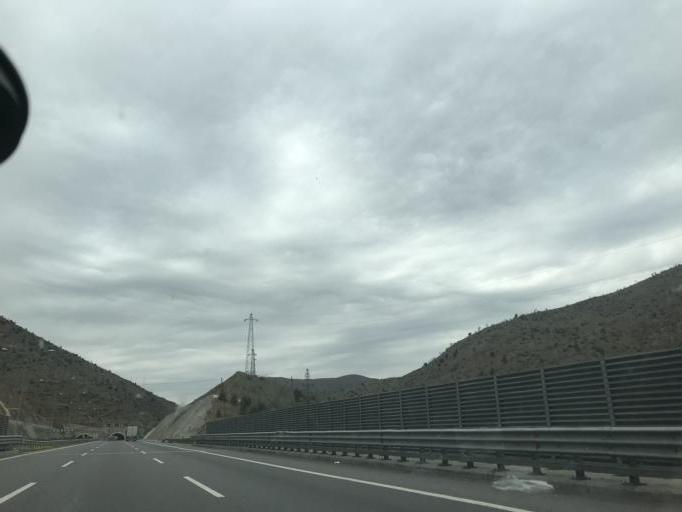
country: TR
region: Nigde
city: Ciftehan
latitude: 37.5689
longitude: 34.7547
